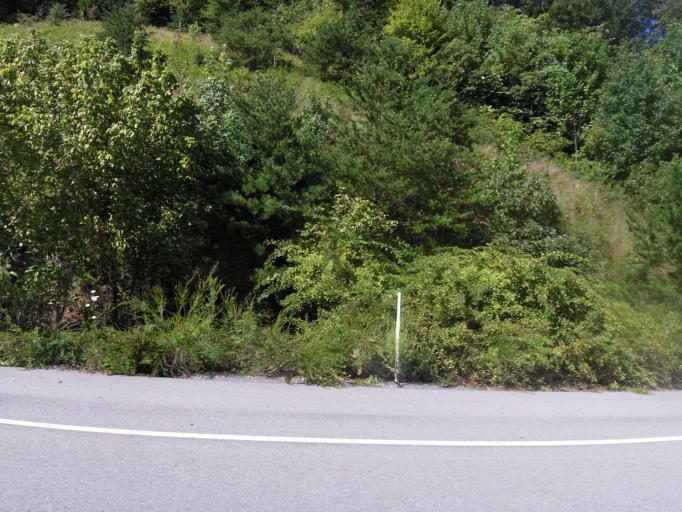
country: US
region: Kentucky
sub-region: Bell County
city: Pineville
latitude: 36.7488
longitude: -83.5967
